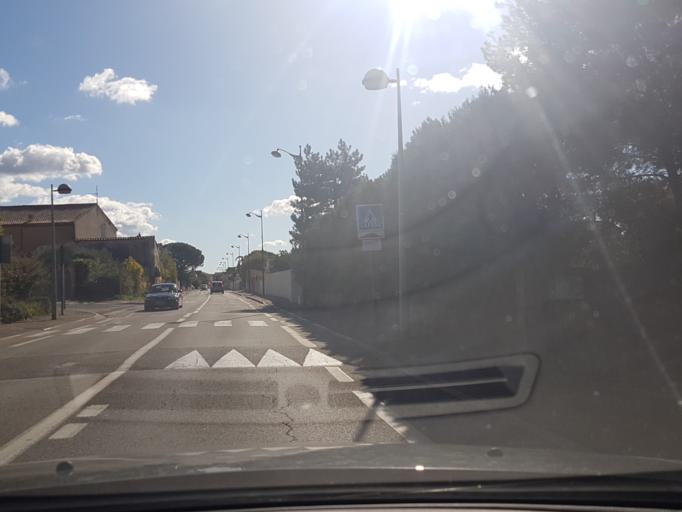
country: FR
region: Provence-Alpes-Cote d'Azur
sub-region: Departement du Vaucluse
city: Morieres-les-Avignon
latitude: 43.9479
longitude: 4.9030
